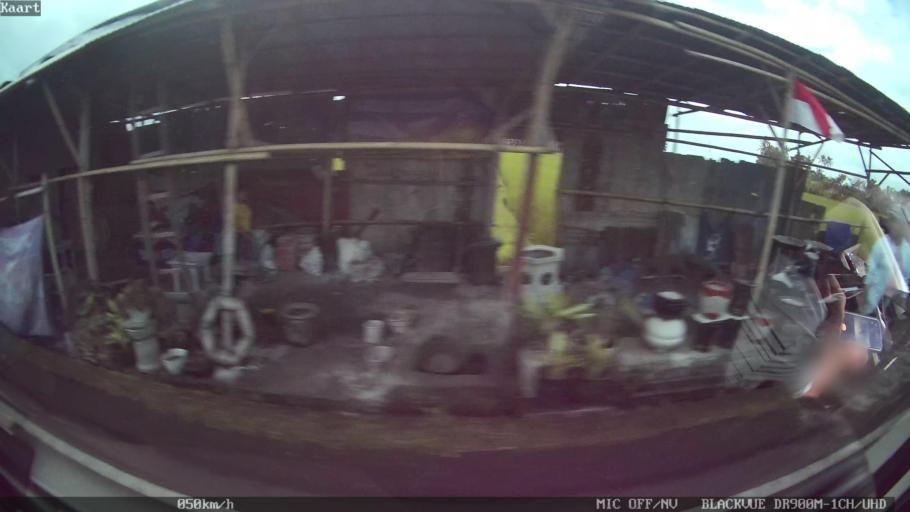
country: ID
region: Bali
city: Banjar Cemenggon
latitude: -8.5605
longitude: 115.1978
